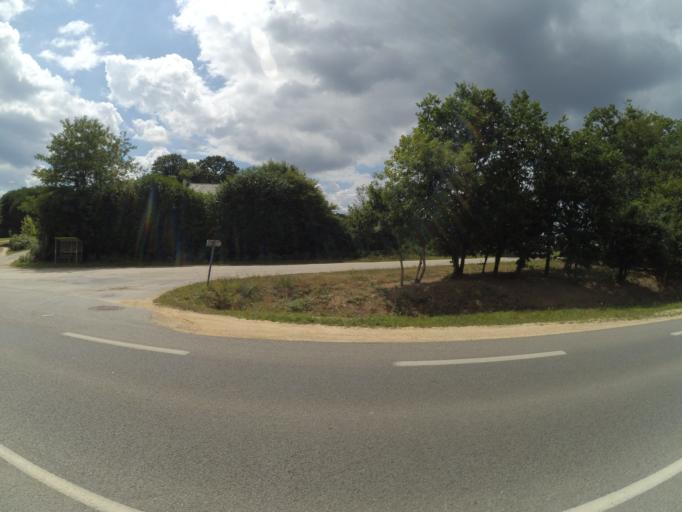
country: FR
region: Brittany
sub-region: Departement du Morbihan
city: Brech
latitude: 47.6995
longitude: -3.0069
